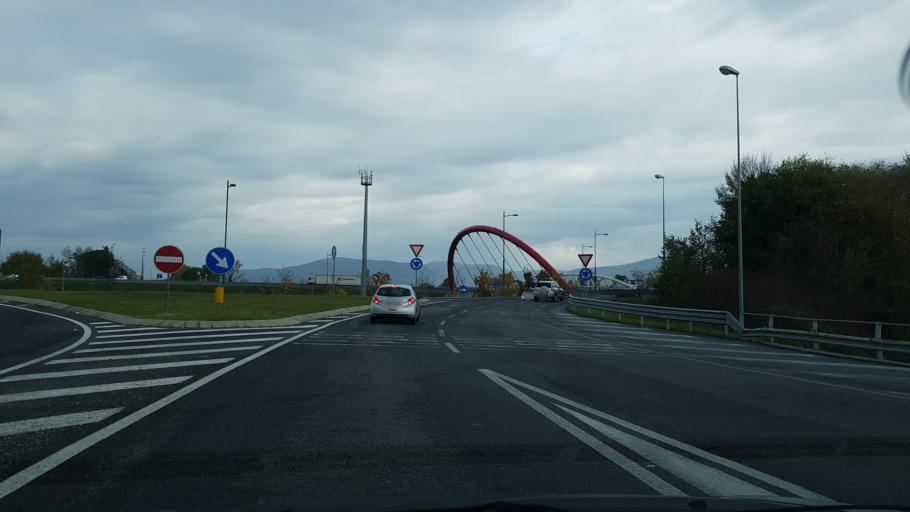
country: SI
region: Sempeter-Vrtojba
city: Vrtojba
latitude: 45.9173
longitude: 13.6136
